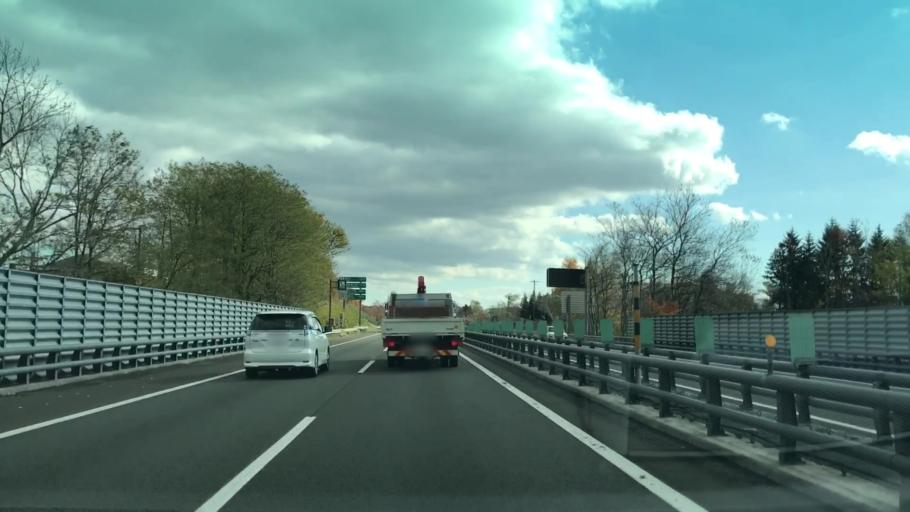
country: JP
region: Hokkaido
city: Kitahiroshima
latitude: 42.9726
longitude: 141.4842
